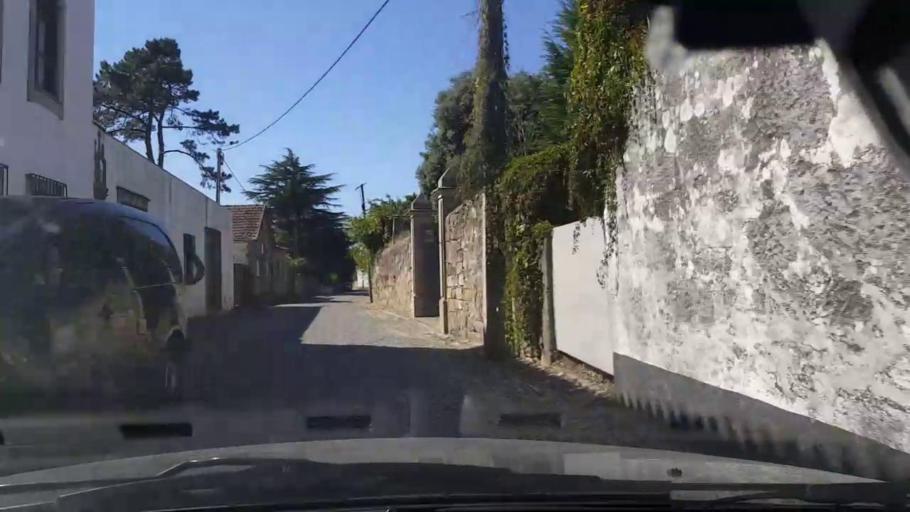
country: PT
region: Porto
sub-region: Maia
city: Gemunde
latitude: 41.2990
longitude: -8.6664
